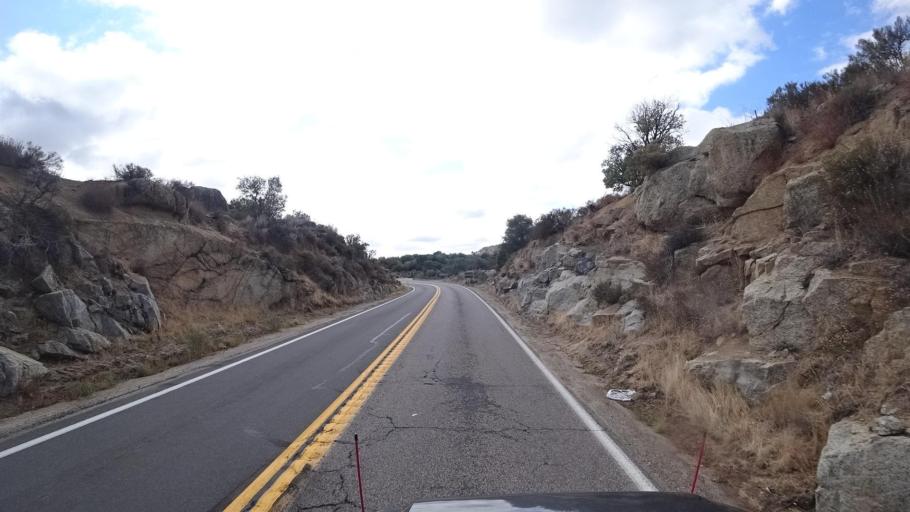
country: US
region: California
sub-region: San Diego County
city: Pine Valley
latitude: 32.7177
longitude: -116.4995
